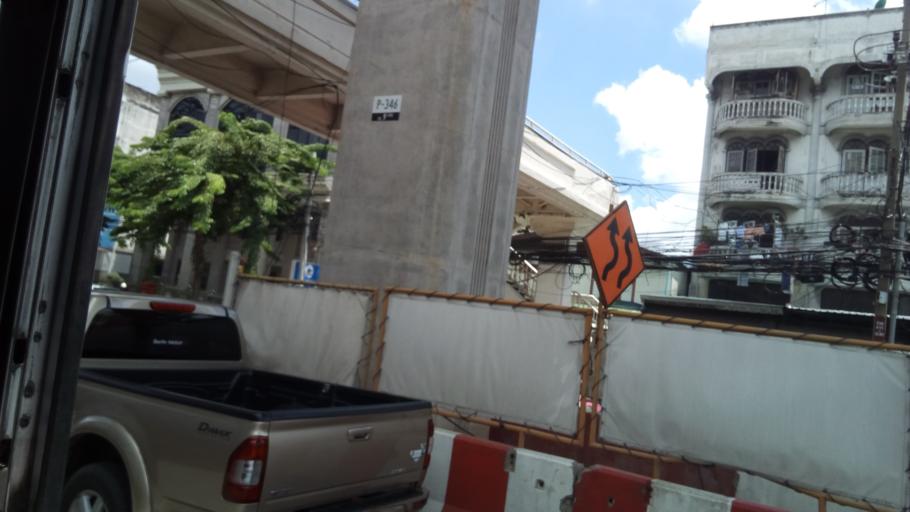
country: TH
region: Bangkok
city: Lak Si
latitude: 13.8835
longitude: 100.6015
